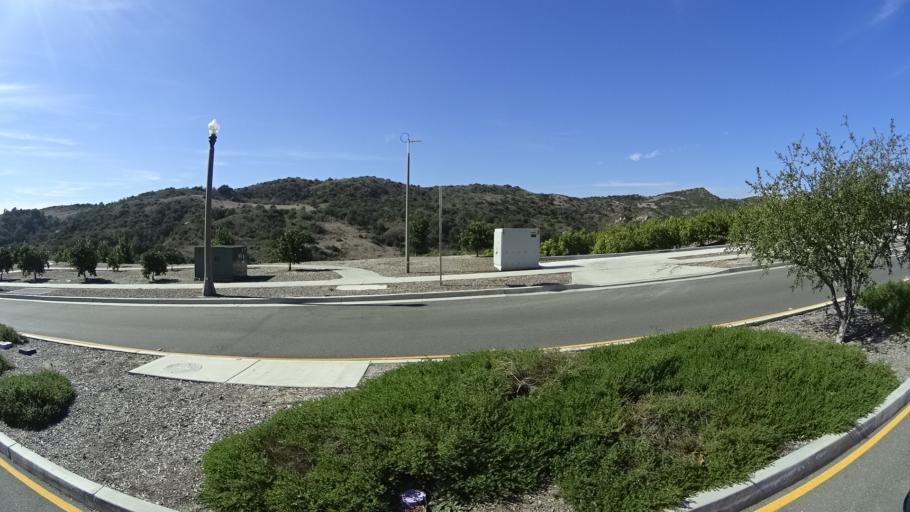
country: US
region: California
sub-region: Orange County
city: Ladera Ranch
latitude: 33.5391
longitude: -117.6075
